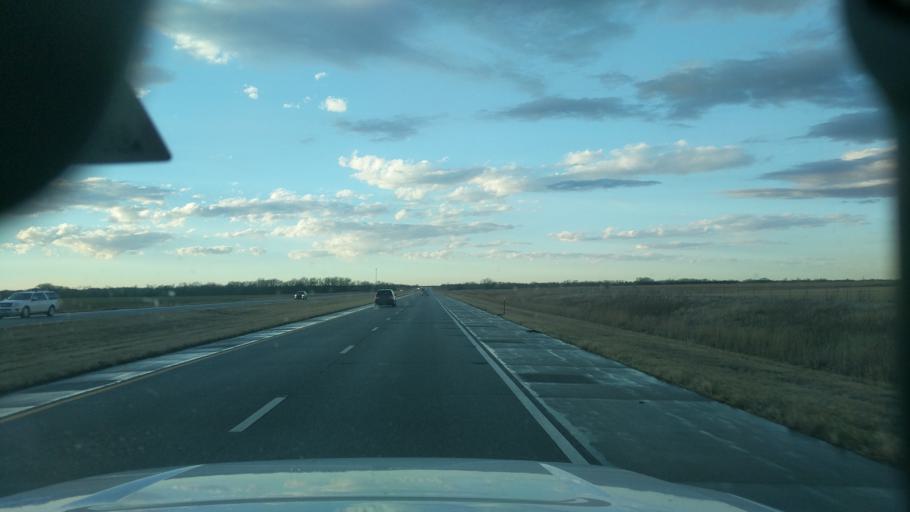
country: US
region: Kansas
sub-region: Harvey County
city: Hesston
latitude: 38.1784
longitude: -97.4533
